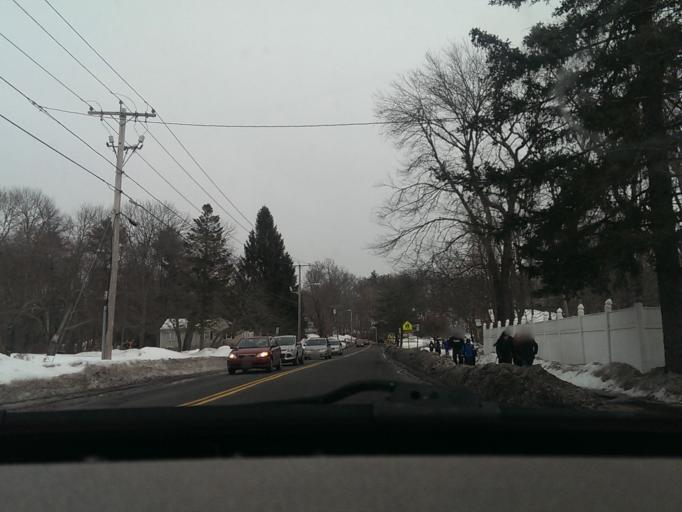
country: US
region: Massachusetts
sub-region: Hampden County
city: East Longmeadow
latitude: 42.0742
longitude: -72.5098
